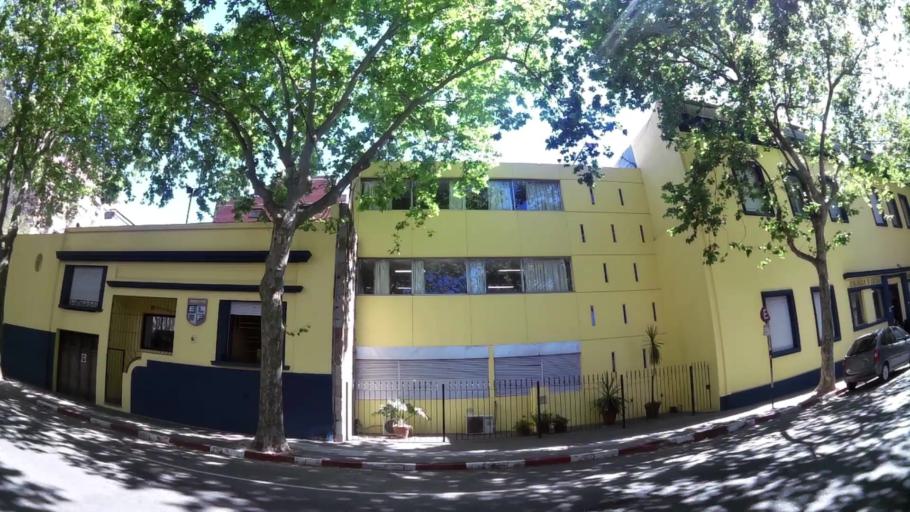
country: UY
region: Montevideo
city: Montevideo
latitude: -34.9093
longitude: -56.1861
